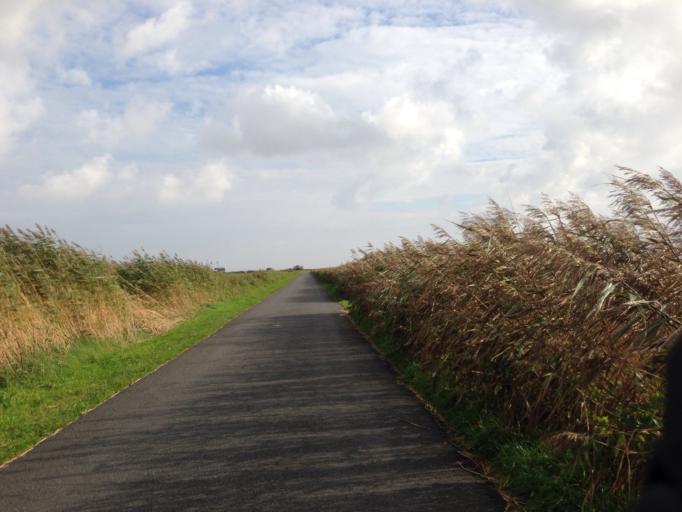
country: DE
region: Schleswig-Holstein
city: Utersum
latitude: 54.7026
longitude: 8.4212
